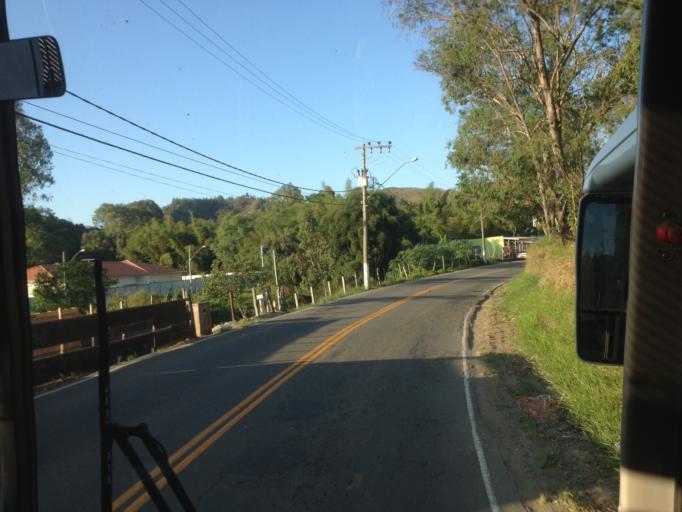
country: BR
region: Minas Gerais
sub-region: Juiz De Fora
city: Juiz de Fora
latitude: -21.6795
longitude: -43.3468
